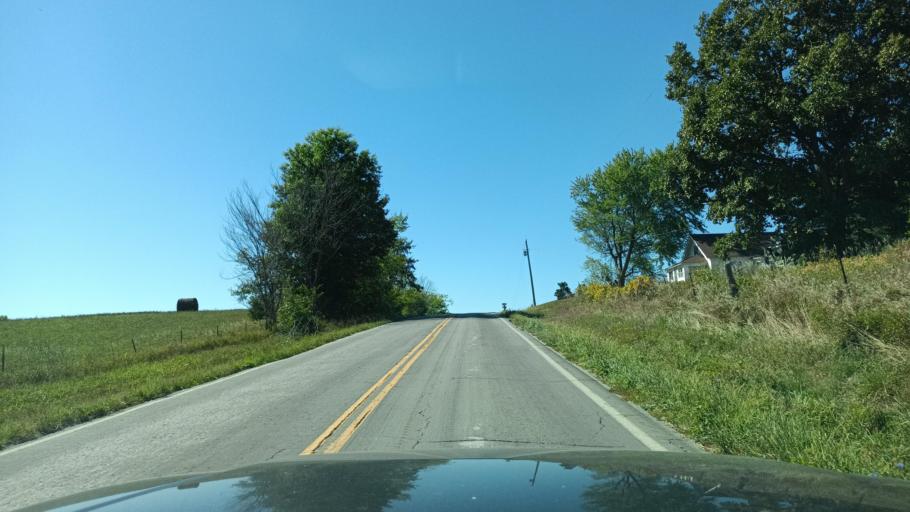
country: US
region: Missouri
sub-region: Macon County
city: La Plata
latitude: 40.0217
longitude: -92.5344
